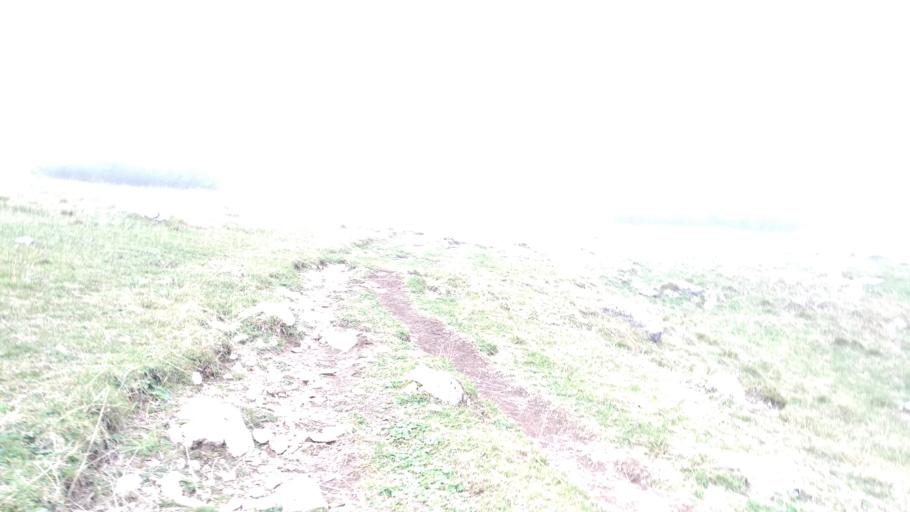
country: IT
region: Veneto
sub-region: Provincia di Vicenza
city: Roana
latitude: 45.9595
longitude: 11.4555
